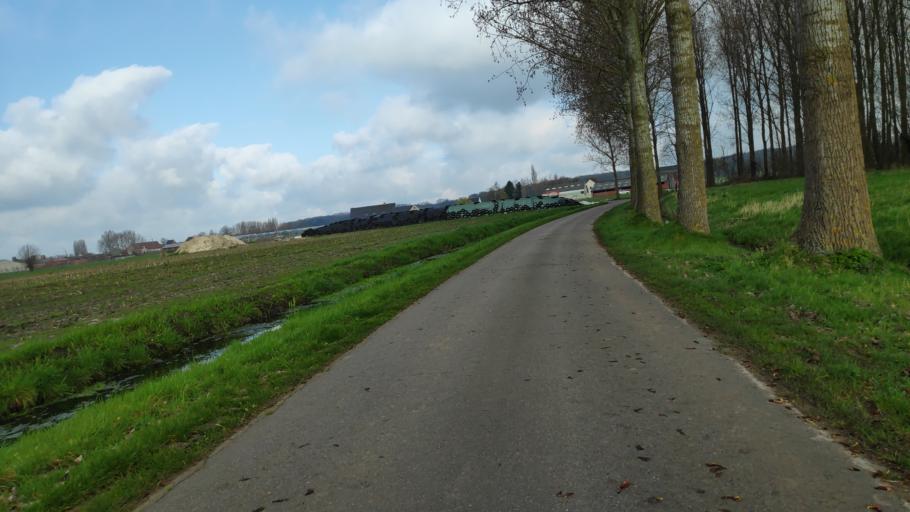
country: BE
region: Flanders
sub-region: Provincie Oost-Vlaanderen
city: Aalter
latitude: 51.1180
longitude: 3.4662
